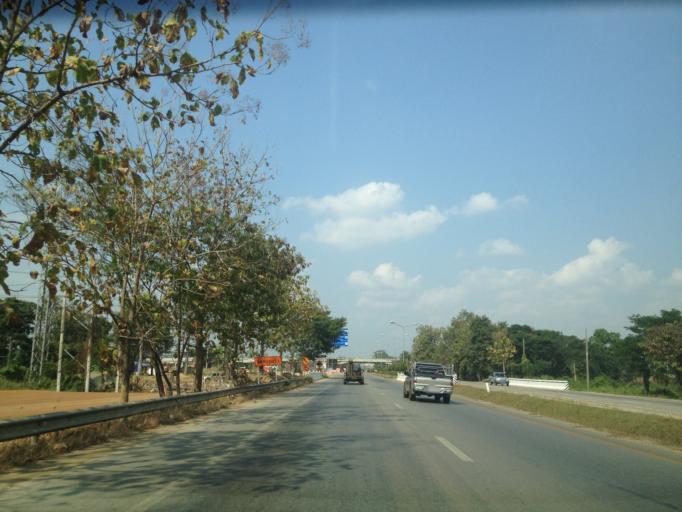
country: TH
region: Chiang Mai
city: Saraphi
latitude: 18.7322
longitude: 99.0384
